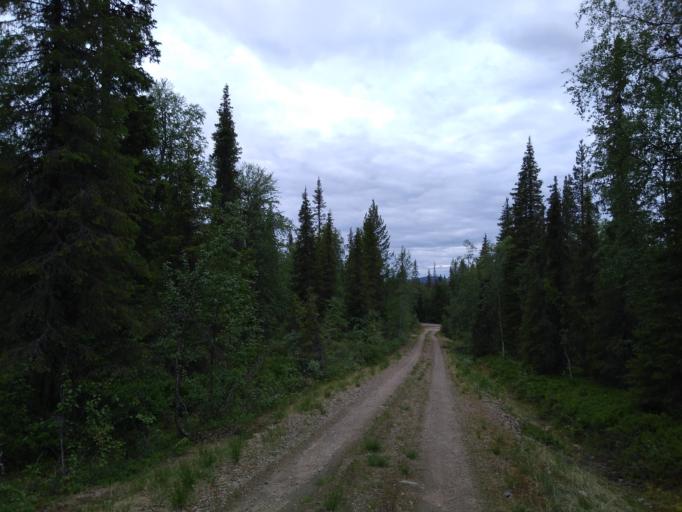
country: FI
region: Lapland
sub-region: Tunturi-Lappi
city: Muonio
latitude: 67.9635
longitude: 24.0758
